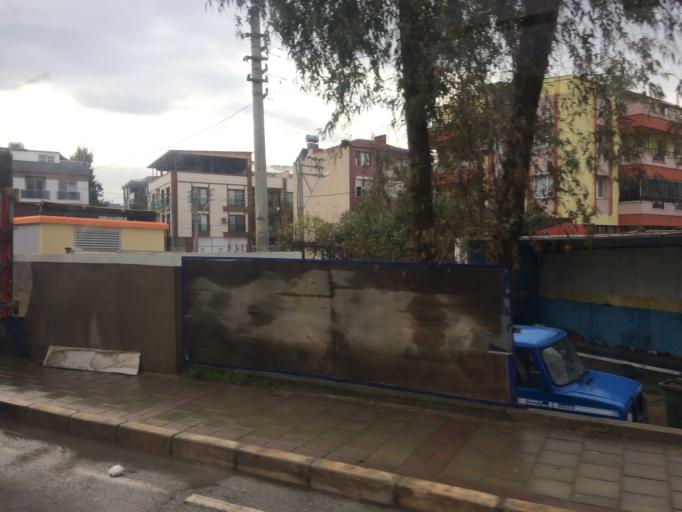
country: TR
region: Izmir
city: Karsiyaka
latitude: 38.5174
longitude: 27.0412
